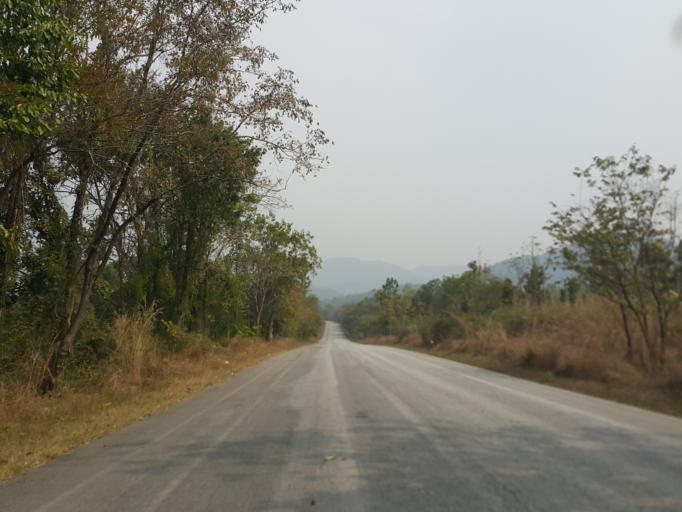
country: TH
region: Lampang
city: Thoen
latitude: 17.6304
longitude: 99.2617
